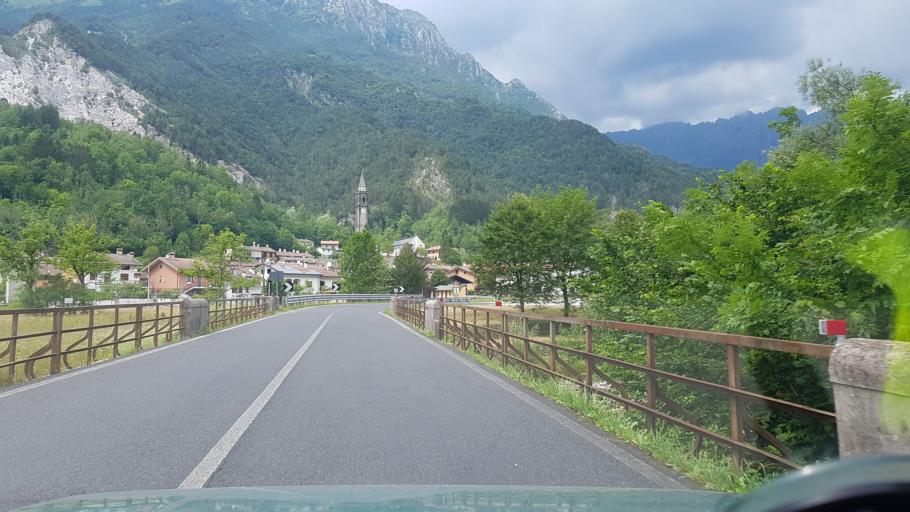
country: IT
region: Friuli Venezia Giulia
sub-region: Provincia di Udine
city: Lusevera
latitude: 46.2766
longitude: 13.2610
